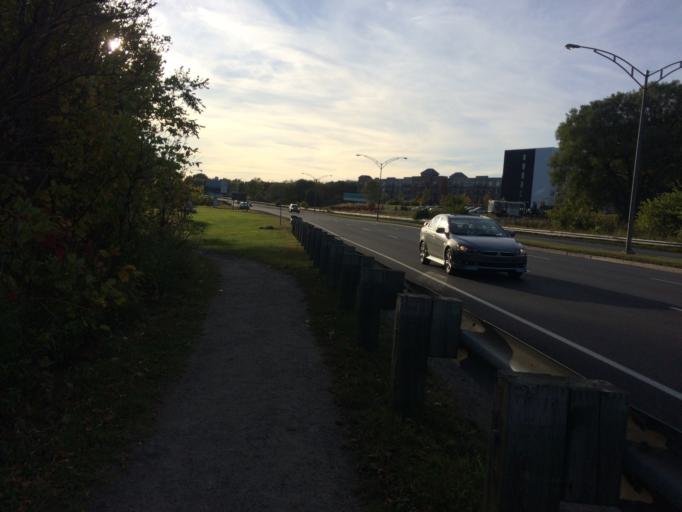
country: CA
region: Quebec
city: Quebec
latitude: 46.8086
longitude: -71.2643
